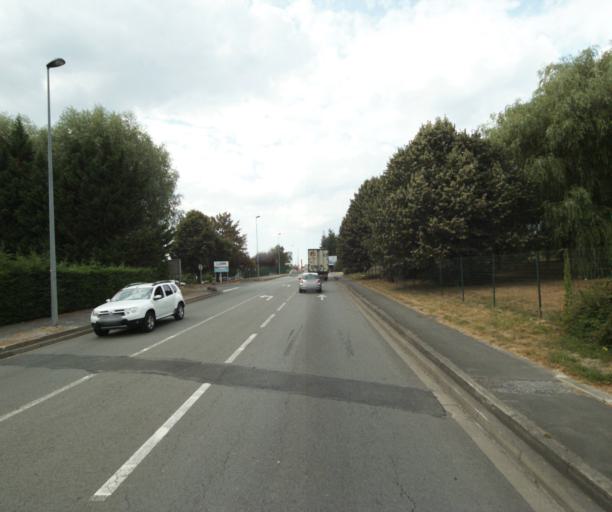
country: FR
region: Nord-Pas-de-Calais
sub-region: Departement du Nord
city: Neuville-en-Ferrain
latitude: 50.7584
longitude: 3.1617
